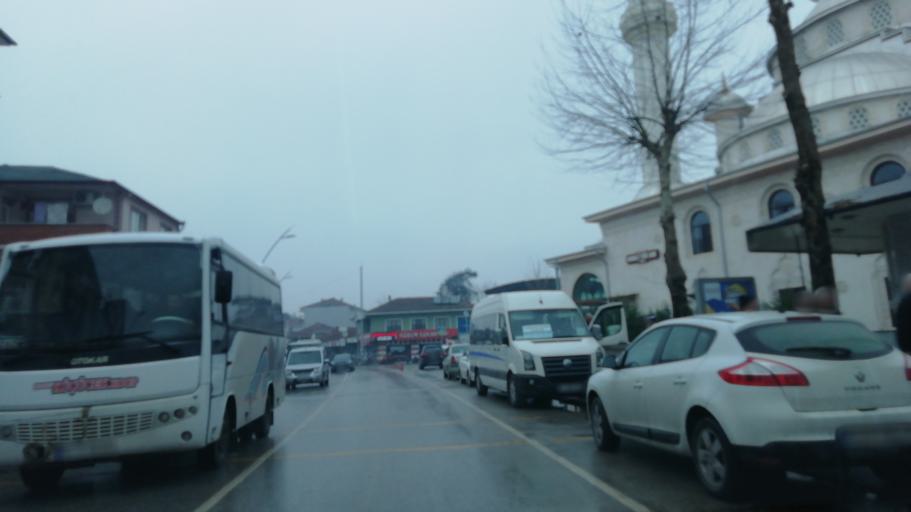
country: TR
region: Sakarya
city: Akyazi
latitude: 40.6869
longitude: 30.6253
